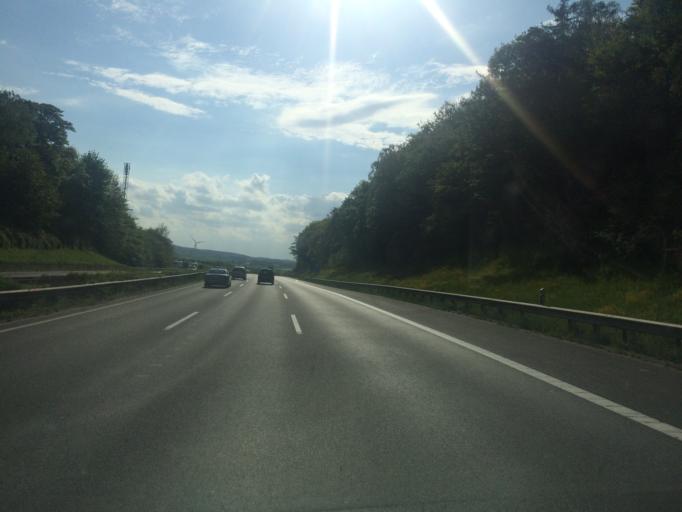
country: DE
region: North Rhine-Westphalia
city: Porta Westfalica
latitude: 52.2127
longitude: 8.9391
